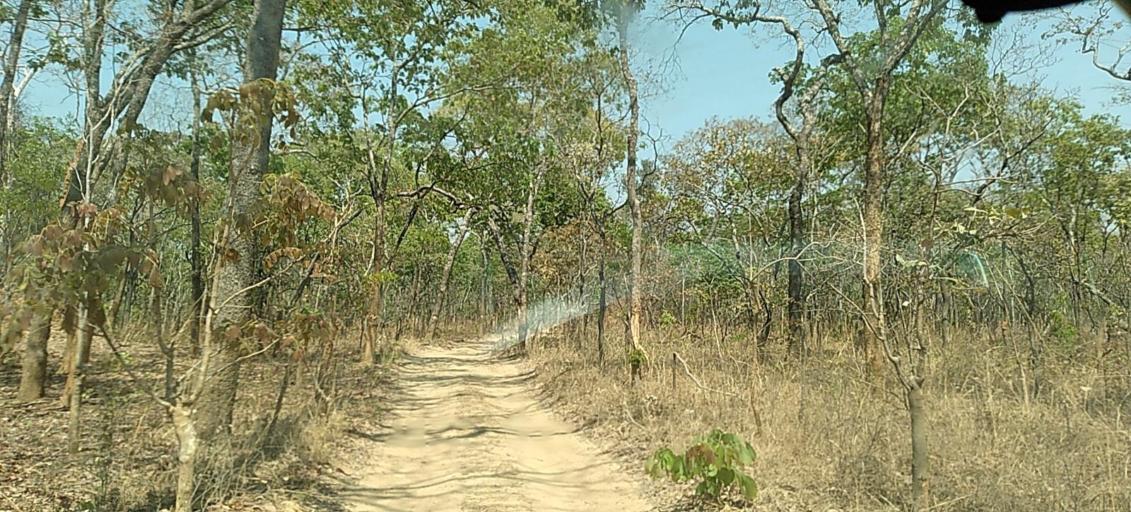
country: ZM
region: North-Western
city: Kasempa
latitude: -13.3920
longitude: 25.6258
